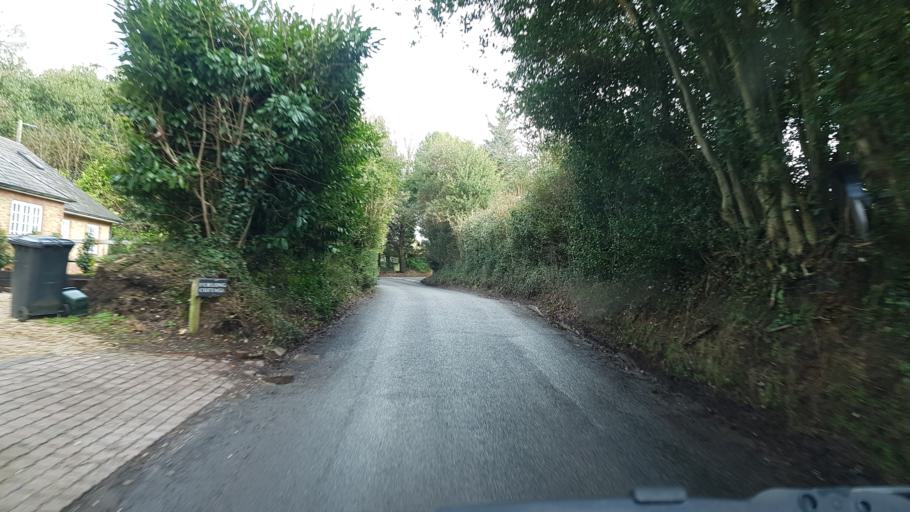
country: GB
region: England
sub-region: Surrey
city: Churt
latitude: 51.1406
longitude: -0.7625
